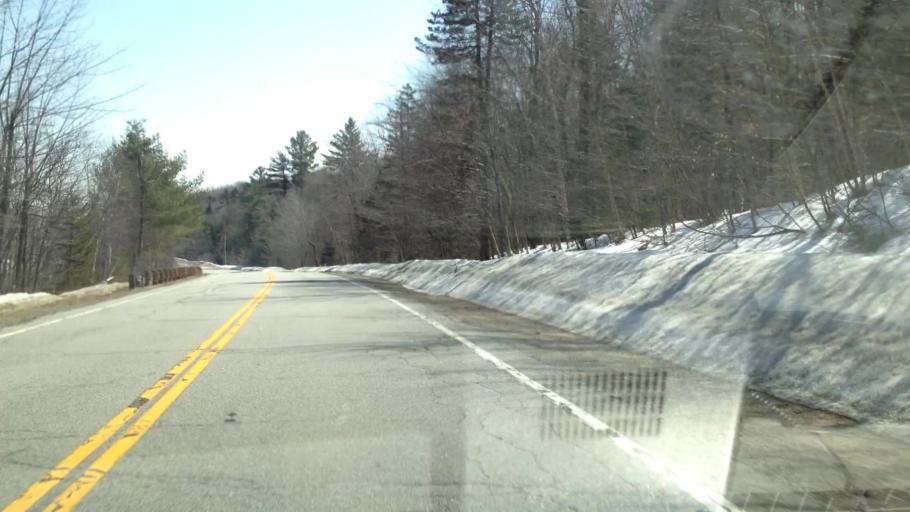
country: US
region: New Hampshire
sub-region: Sullivan County
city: Springfield
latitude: 43.4981
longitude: -72.0108
